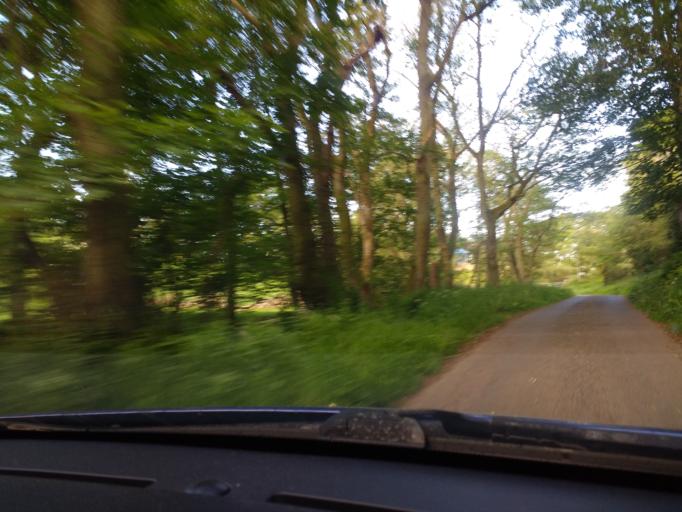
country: GB
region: England
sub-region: Cumbria
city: Appleby-in-Westmorland
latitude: 54.6770
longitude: -2.5640
